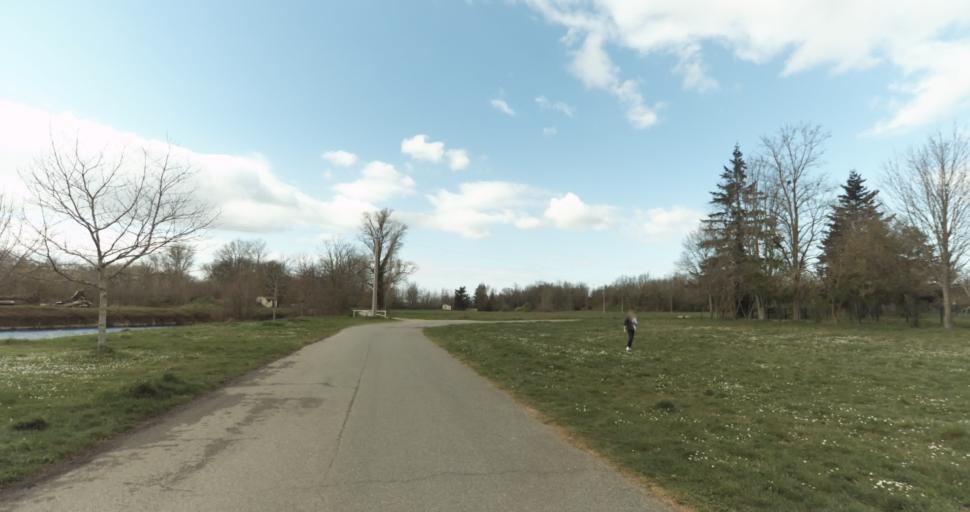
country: FR
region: Midi-Pyrenees
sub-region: Departement de la Haute-Garonne
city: Auterive
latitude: 43.3394
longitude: 1.4830
